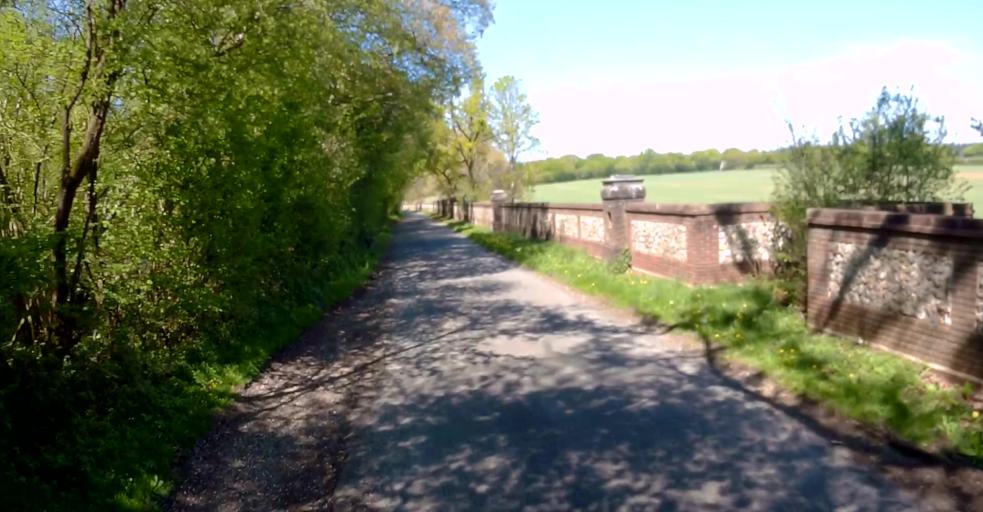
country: GB
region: England
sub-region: Hampshire
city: Overton
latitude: 51.2008
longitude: -1.2839
